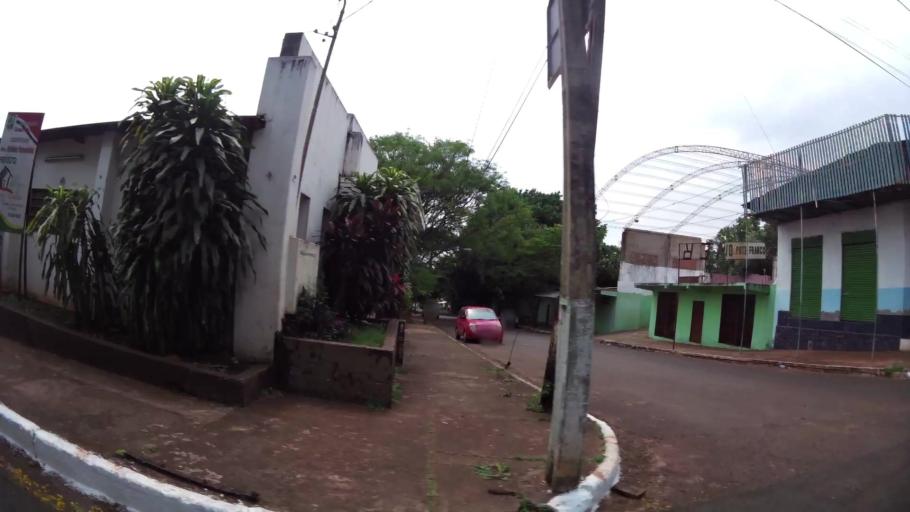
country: BR
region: Parana
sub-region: Foz Do Iguacu
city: Foz do Iguacu
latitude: -25.5537
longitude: -54.6062
